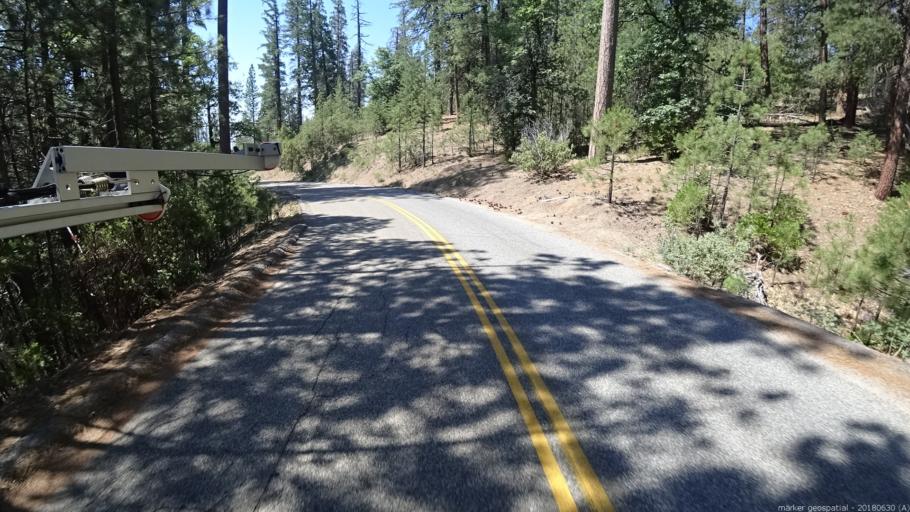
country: US
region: California
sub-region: Madera County
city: Oakhurst
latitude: 37.3967
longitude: -119.3519
